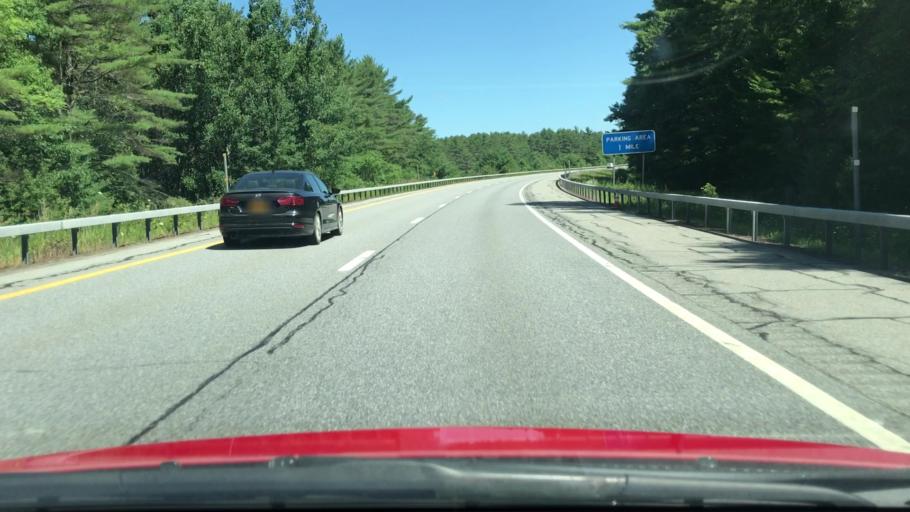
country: US
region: New York
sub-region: Warren County
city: Warrensburg
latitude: 43.5333
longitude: -73.7404
